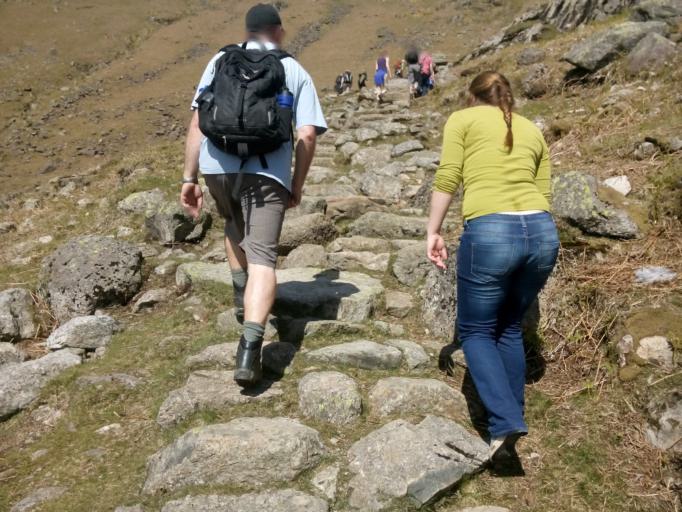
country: GB
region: England
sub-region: Cumbria
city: Ambleside
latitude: 54.4552
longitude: -3.0981
